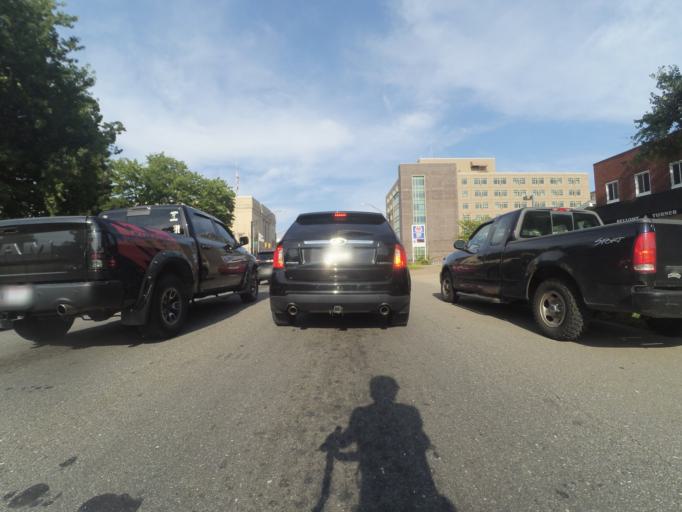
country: US
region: West Virginia
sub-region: Cabell County
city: Huntington
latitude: 38.4190
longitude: -82.4460
